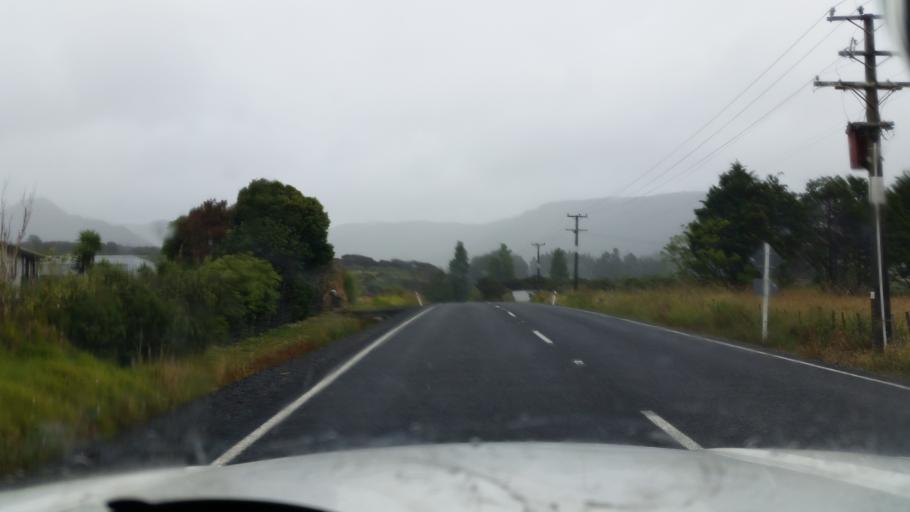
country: NZ
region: Northland
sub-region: Far North District
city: Ahipara
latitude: -35.1799
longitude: 173.1685
